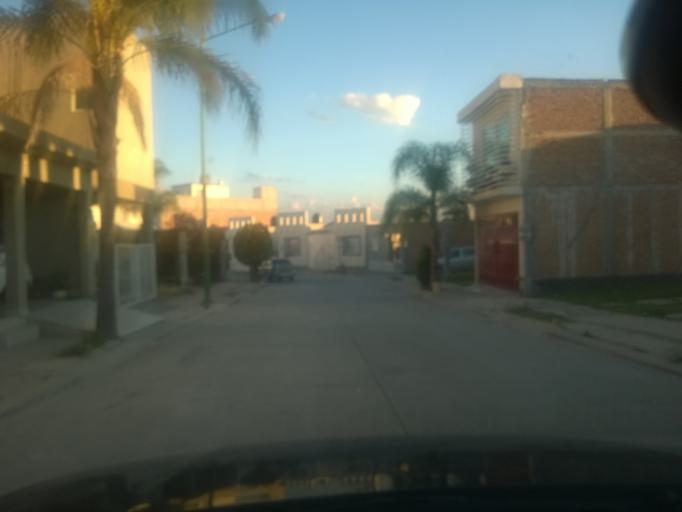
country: MX
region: Guanajuato
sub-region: Leon
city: La Ermita
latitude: 21.1556
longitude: -101.7463
